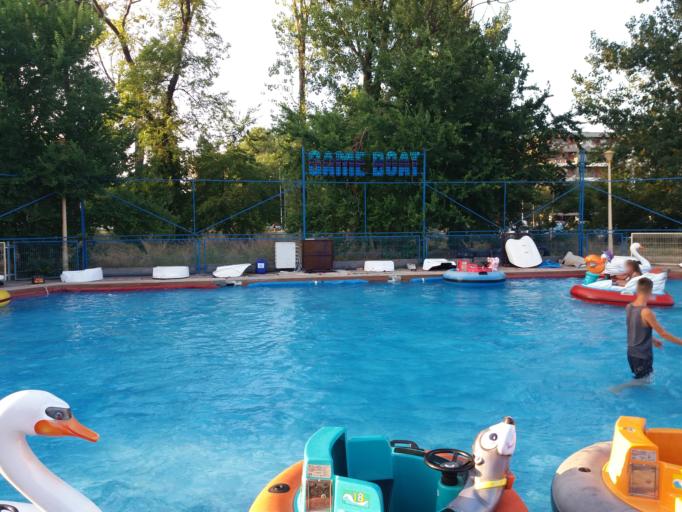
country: RO
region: Constanta
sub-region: Municipiul Constanta
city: Palazu Mare
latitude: 44.2177
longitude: 28.6330
